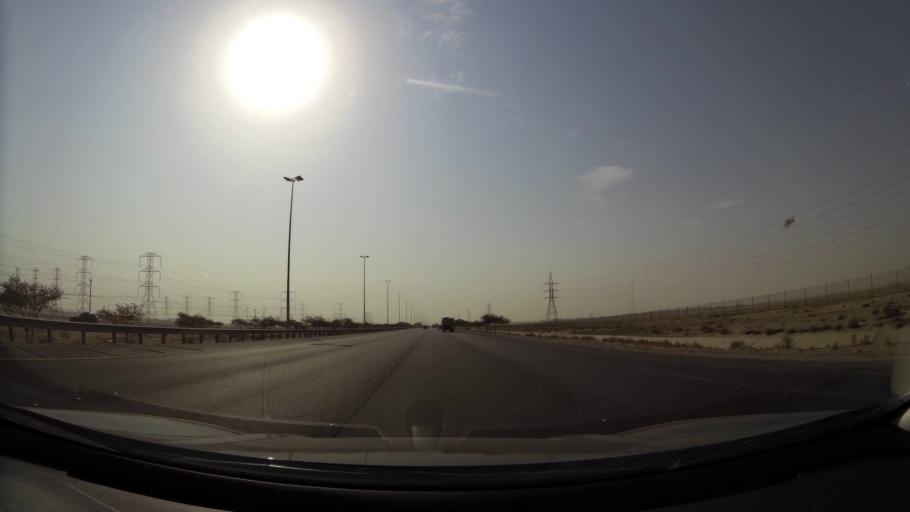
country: KW
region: Al Ahmadi
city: Al Ahmadi
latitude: 28.9862
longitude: 48.1049
